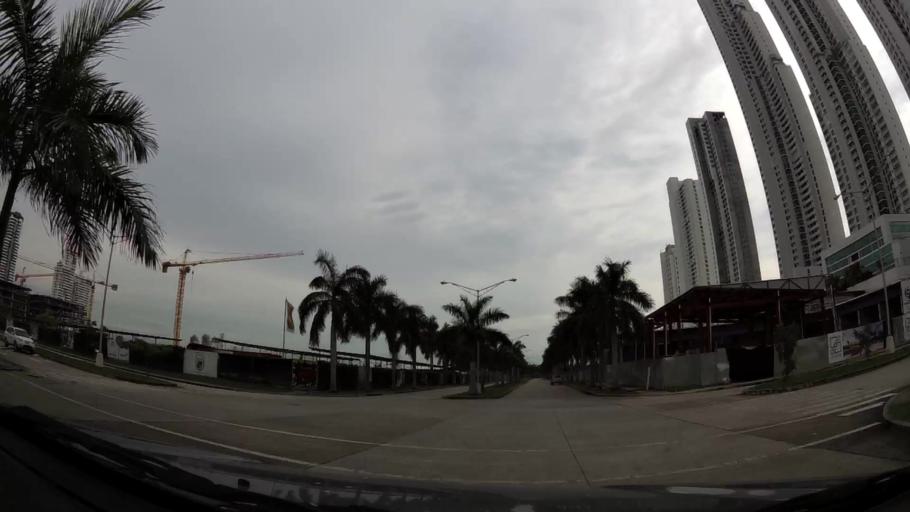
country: PA
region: Panama
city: San Miguelito
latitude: 9.0116
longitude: -79.4656
